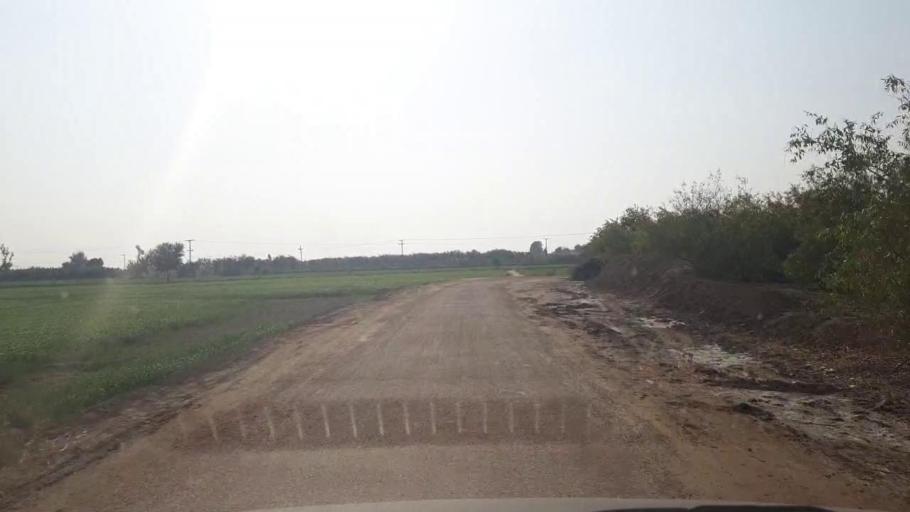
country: PK
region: Sindh
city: Bhit Shah
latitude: 25.8129
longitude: 68.5737
